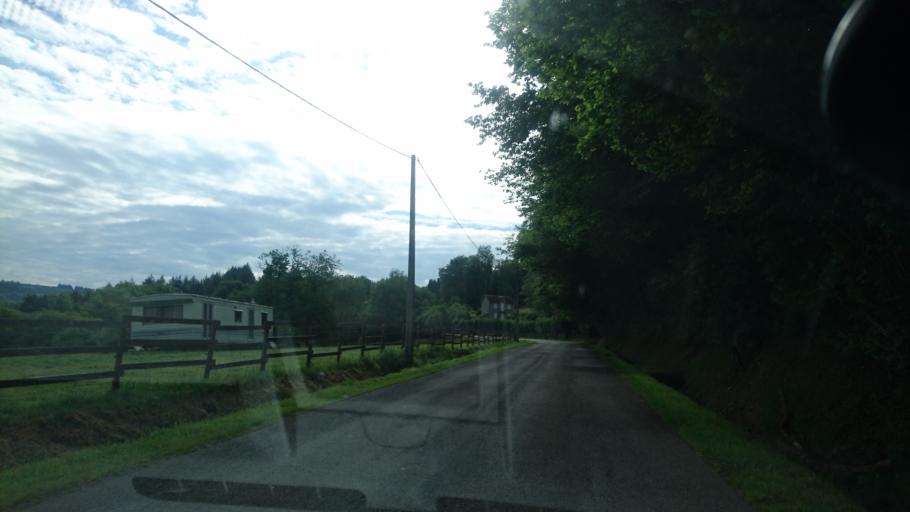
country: FR
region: Limousin
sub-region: Departement de la Haute-Vienne
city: Peyrat-le-Chateau
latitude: 45.8113
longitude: 1.7820
